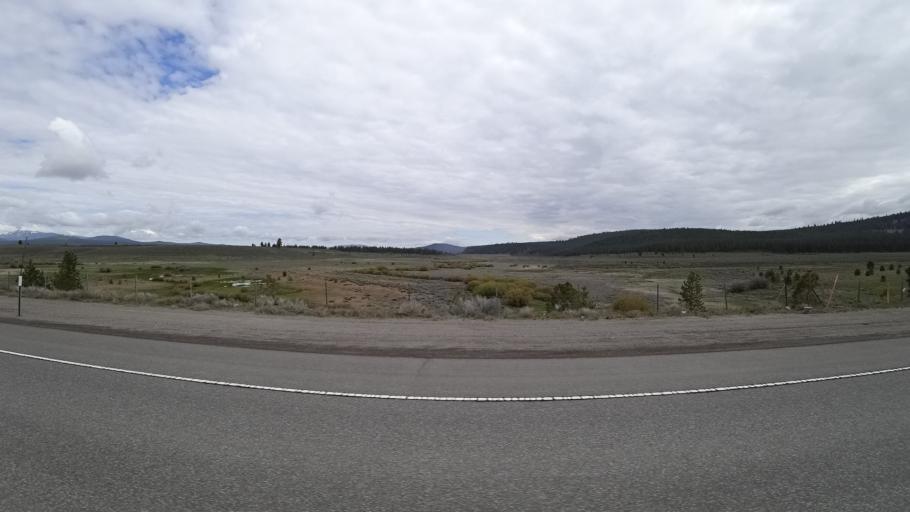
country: US
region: California
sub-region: Nevada County
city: Truckee
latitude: 39.3026
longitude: -120.1208
